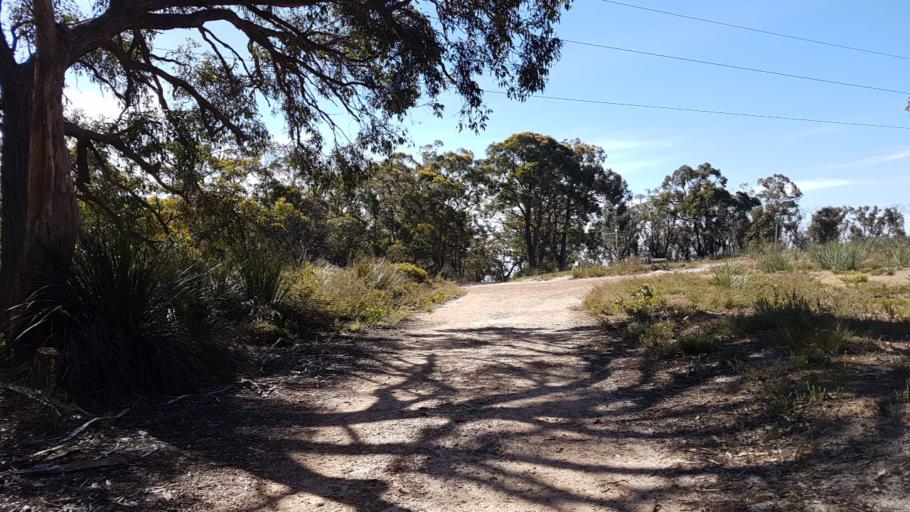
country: AU
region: South Australia
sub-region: Adelaide Hills
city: Adelaide Hills
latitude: -34.8990
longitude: 138.7219
